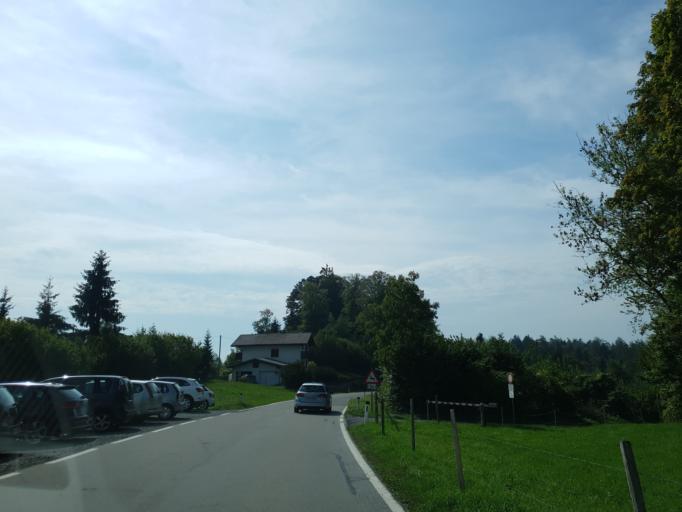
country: AT
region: Vorarlberg
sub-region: Politischer Bezirk Bregenz
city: Kennelbach
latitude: 47.4912
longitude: 9.7695
